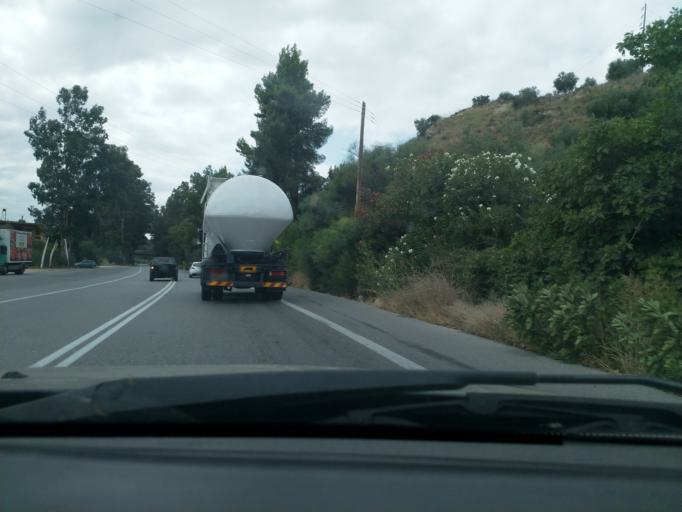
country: GR
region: Crete
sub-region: Nomos Chanias
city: Georgioupolis
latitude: 35.3787
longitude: 24.2050
